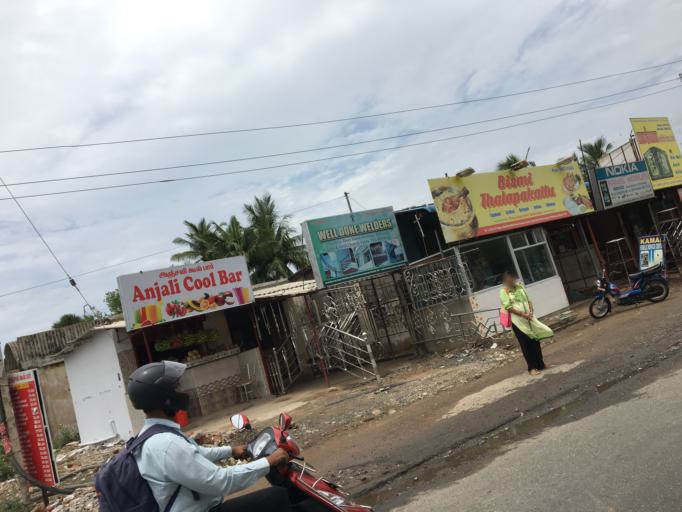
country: IN
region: Tamil Nadu
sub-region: Kancheepuram
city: Madipakkam
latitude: 12.9442
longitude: 80.2083
